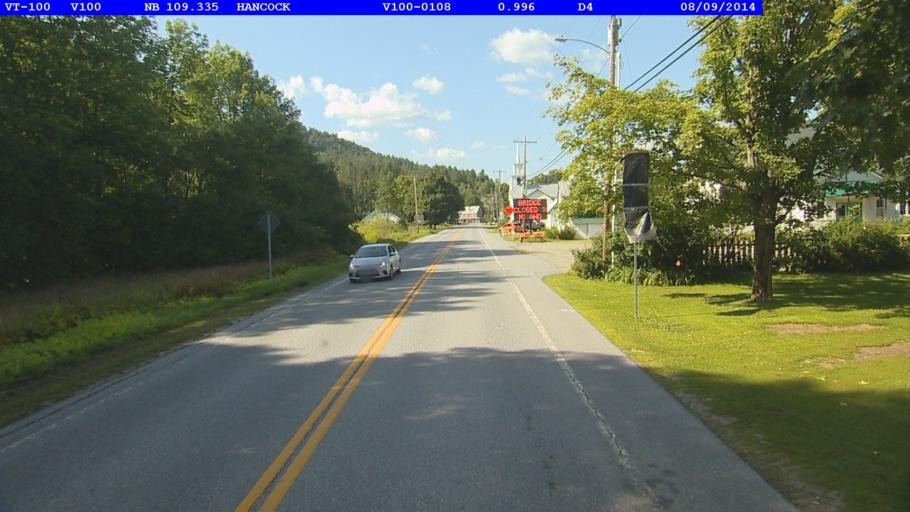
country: US
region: Vermont
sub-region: Orange County
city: Randolph
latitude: 43.9232
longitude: -72.8405
